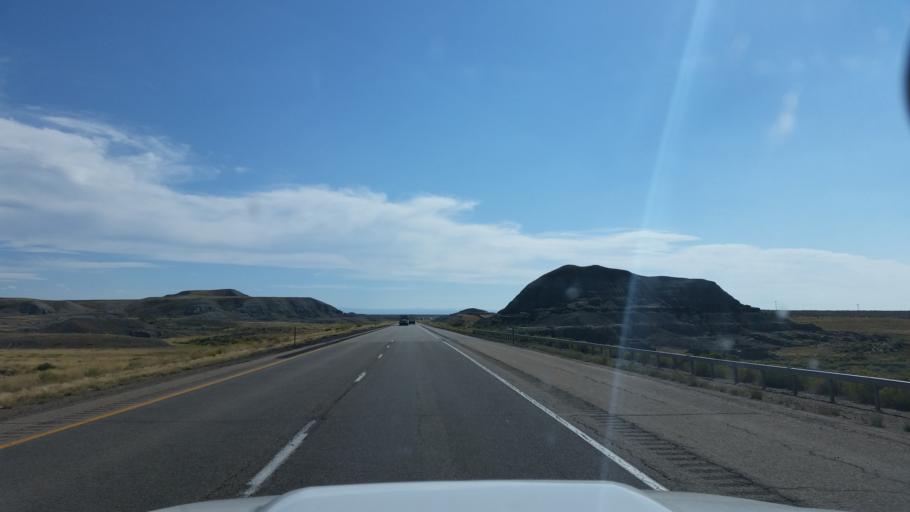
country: US
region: Wyoming
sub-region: Uinta County
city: Lyman
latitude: 41.4208
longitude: -110.1367
